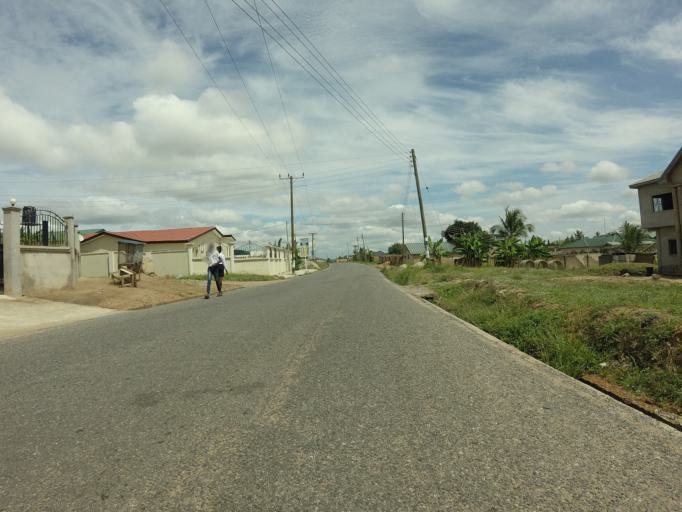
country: GH
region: Central
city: Kasoa
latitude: 5.5244
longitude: -0.4502
